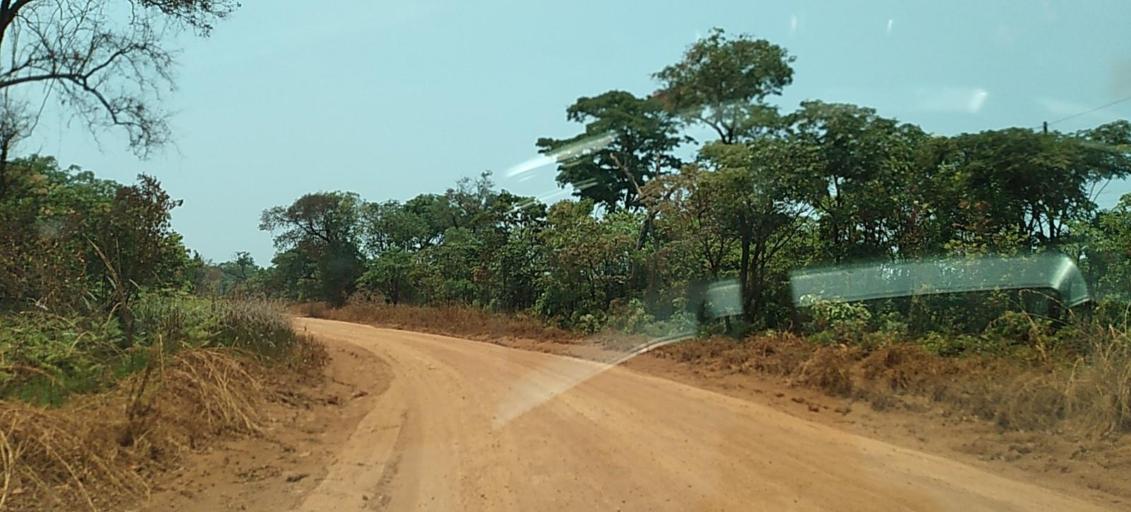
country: CD
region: Katanga
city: Kipushi
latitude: -11.9257
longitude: 27.0127
